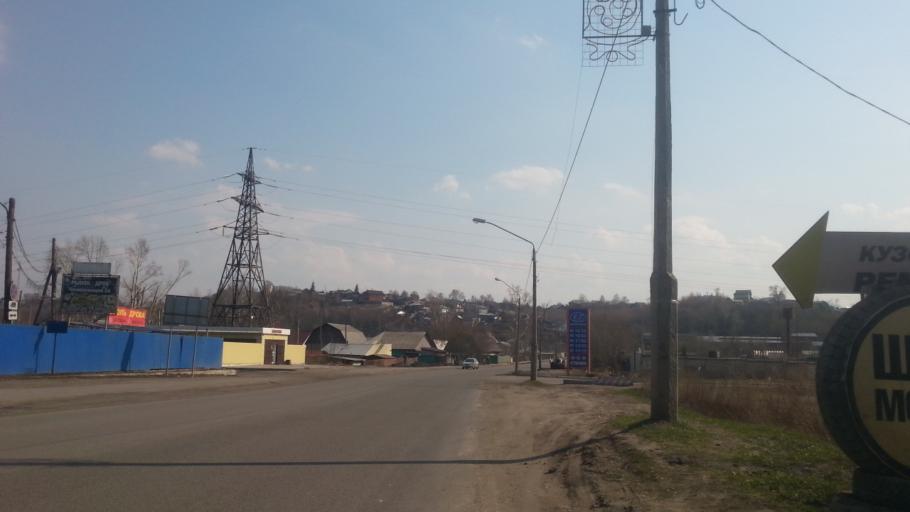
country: RU
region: Altai Krai
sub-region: Gorod Barnaulskiy
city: Barnaul
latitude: 53.3223
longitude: 83.7683
